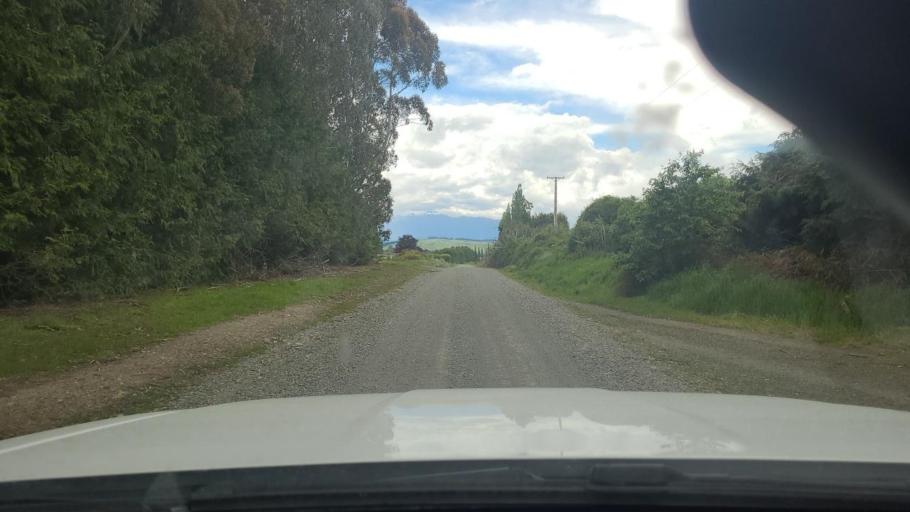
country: NZ
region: Southland
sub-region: Southland District
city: Te Anau
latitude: -45.5603
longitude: 167.7771
